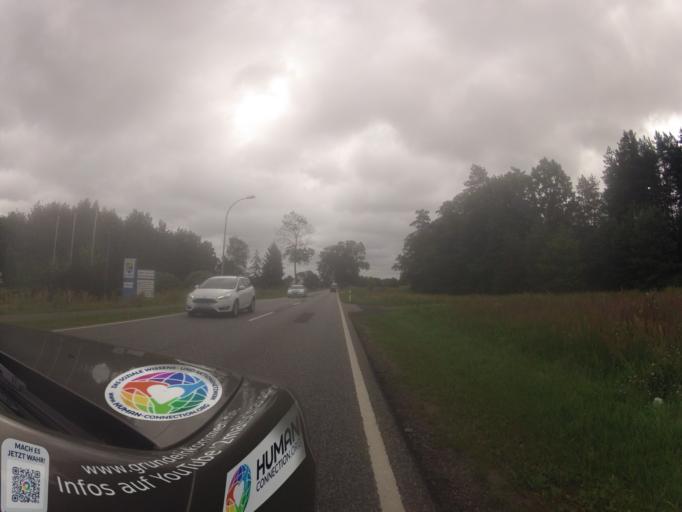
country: DE
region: Mecklenburg-Vorpommern
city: Jatznick
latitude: 53.5679
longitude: 13.9552
